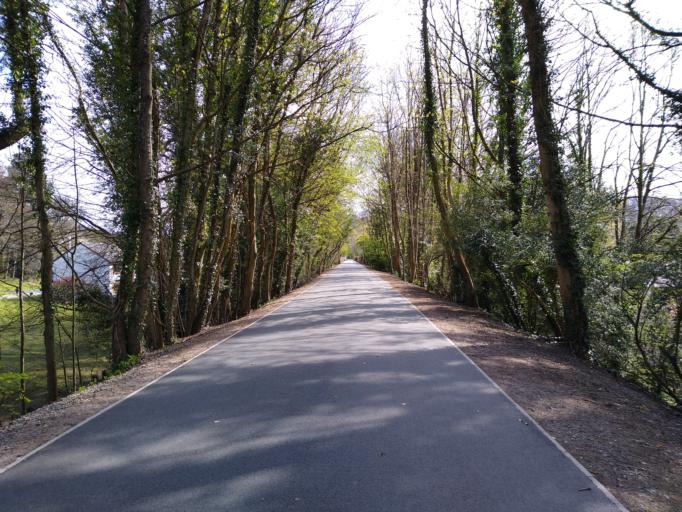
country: GB
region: England
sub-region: Cumbria
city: Keswick
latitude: 54.6037
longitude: -3.1284
